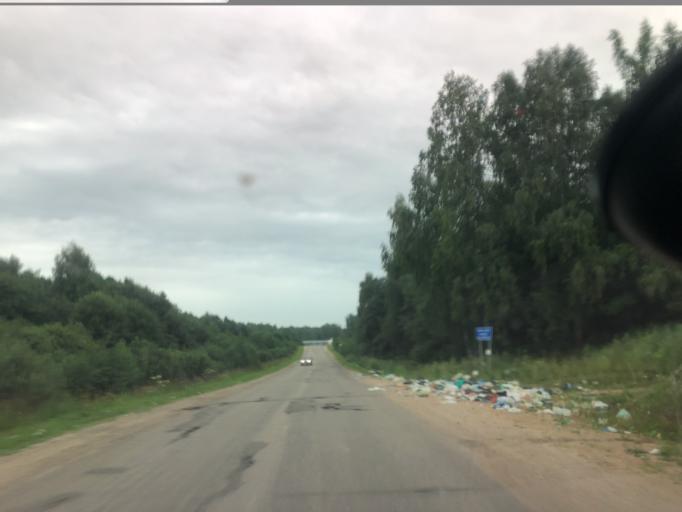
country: RU
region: Jaroslavl
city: Petrovsk
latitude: 56.9842
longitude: 39.2137
